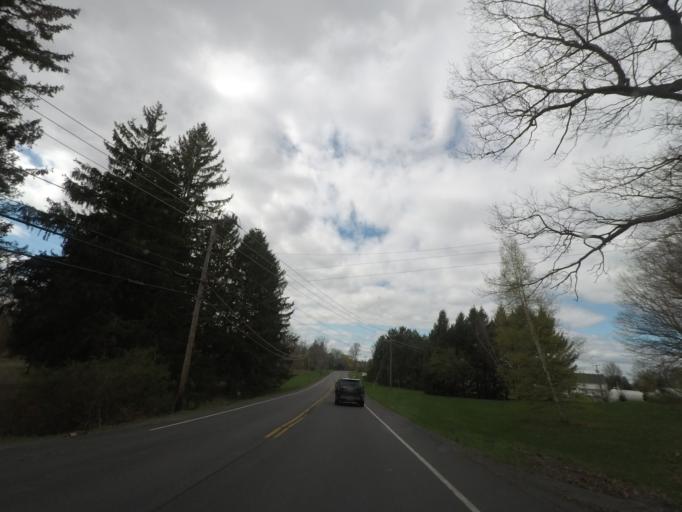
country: US
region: New York
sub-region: Columbia County
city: Chatham
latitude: 42.3656
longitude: -73.6173
